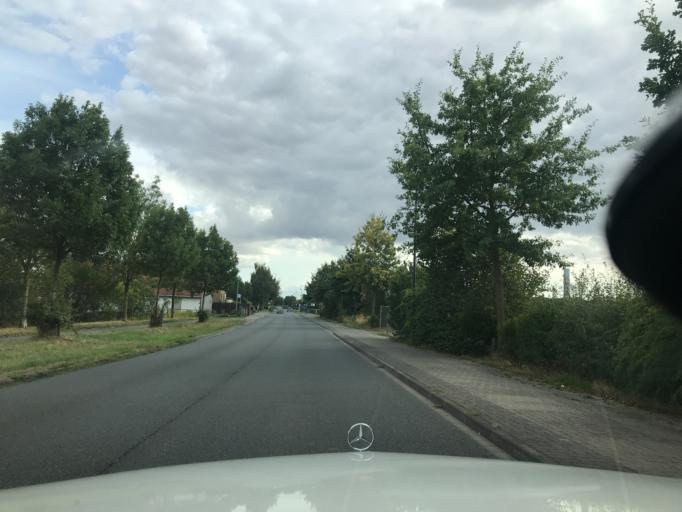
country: DE
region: North Rhine-Westphalia
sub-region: Regierungsbezirk Arnsberg
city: Lippstadt
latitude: 51.6573
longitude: 8.3556
